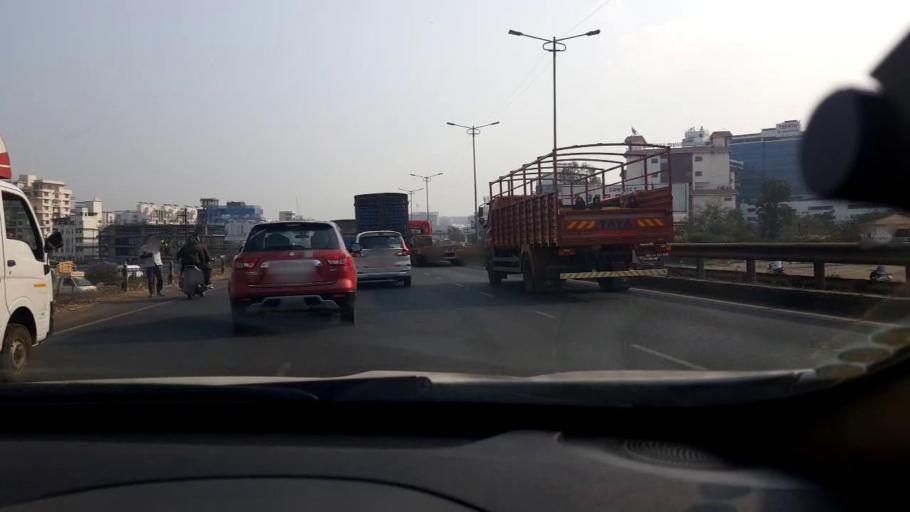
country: IN
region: Maharashtra
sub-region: Pune Division
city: Pimpri
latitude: 18.5665
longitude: 73.7668
